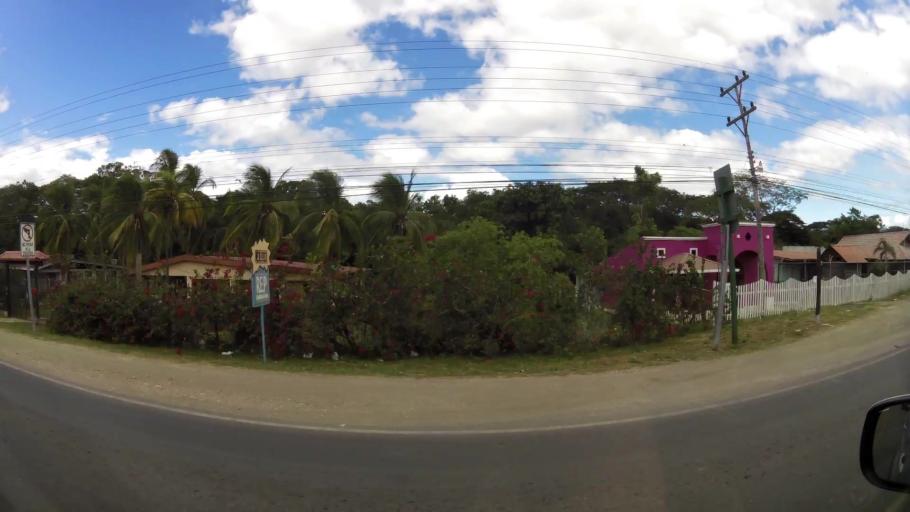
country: CR
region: Guanacaste
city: Santa Cruz
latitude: 10.2678
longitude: -85.5858
